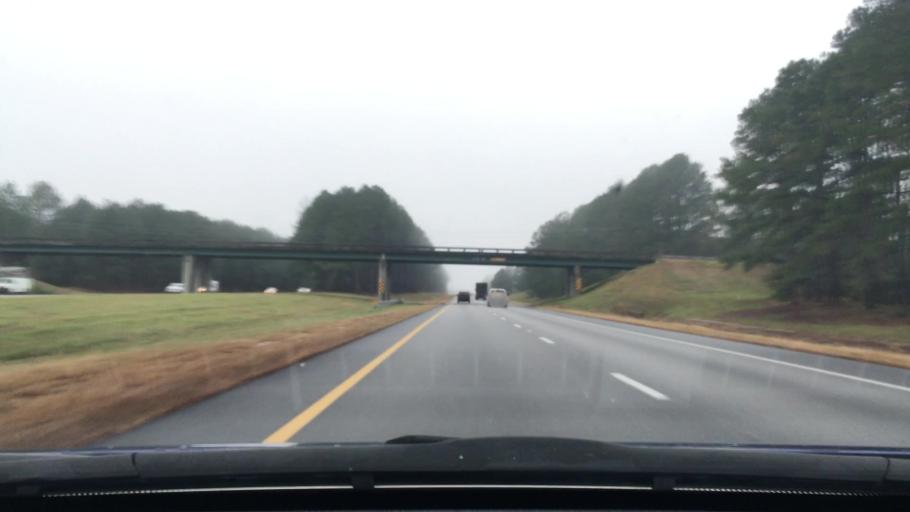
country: US
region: South Carolina
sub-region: Lee County
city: Bishopville
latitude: 34.2037
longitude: -80.3717
